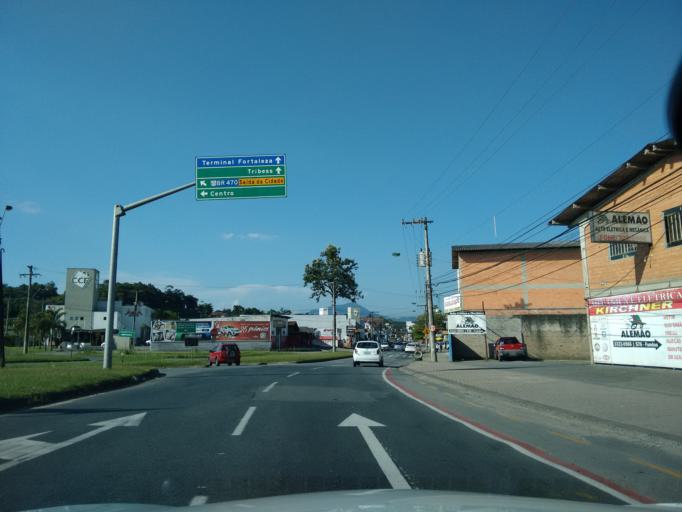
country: BR
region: Santa Catarina
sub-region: Blumenau
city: Blumenau
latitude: -26.8820
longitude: -49.0689
